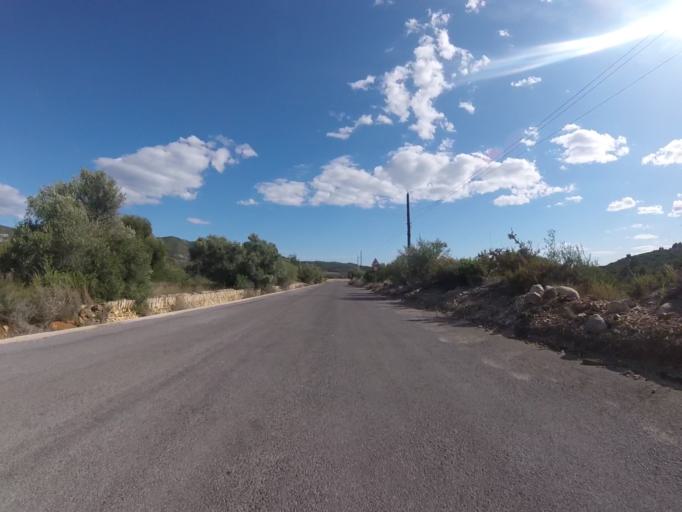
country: ES
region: Valencia
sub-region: Provincia de Castello
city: Alcala de Xivert
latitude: 40.2704
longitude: 0.2395
